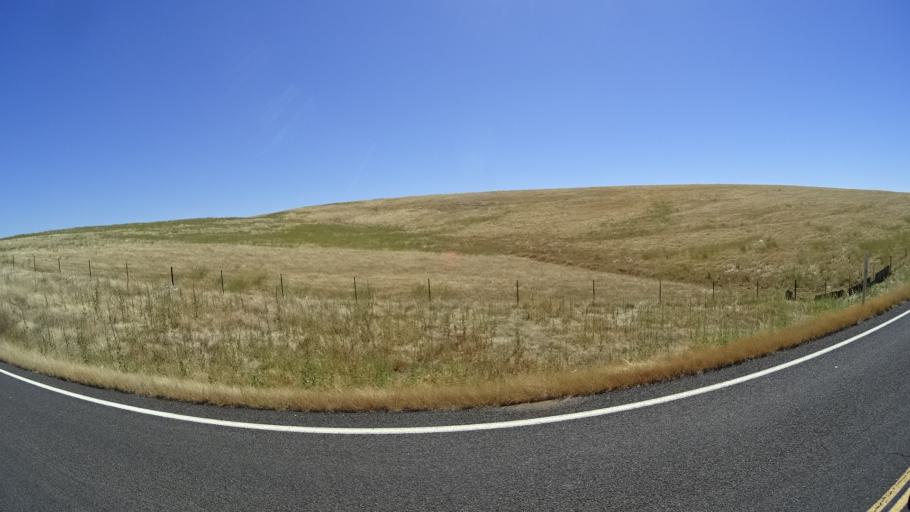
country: US
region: California
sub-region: Calaveras County
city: Rancho Calaveras
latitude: 38.0446
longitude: -120.8594
